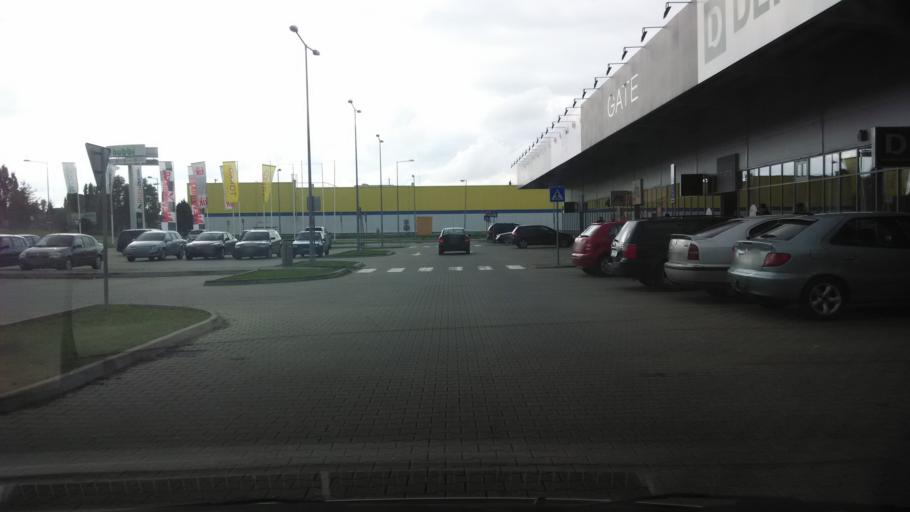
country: SK
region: Nitriansky
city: Levice
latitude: 48.2269
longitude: 18.5980
